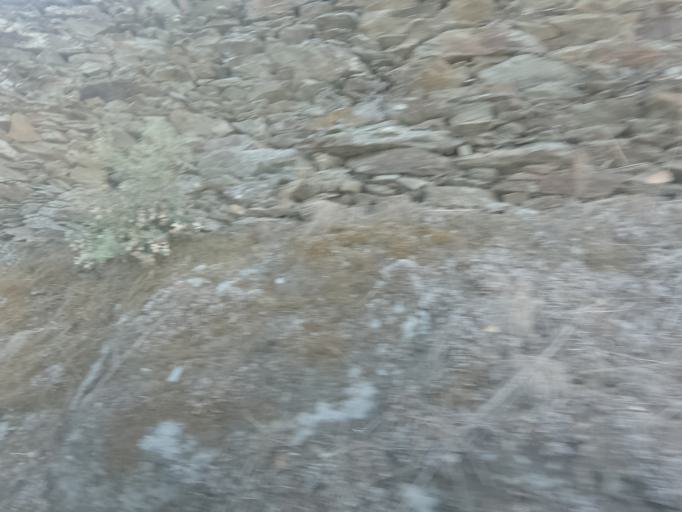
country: PT
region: Viseu
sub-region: Tabuaco
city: Tabuaco
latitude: 41.1492
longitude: -7.6011
